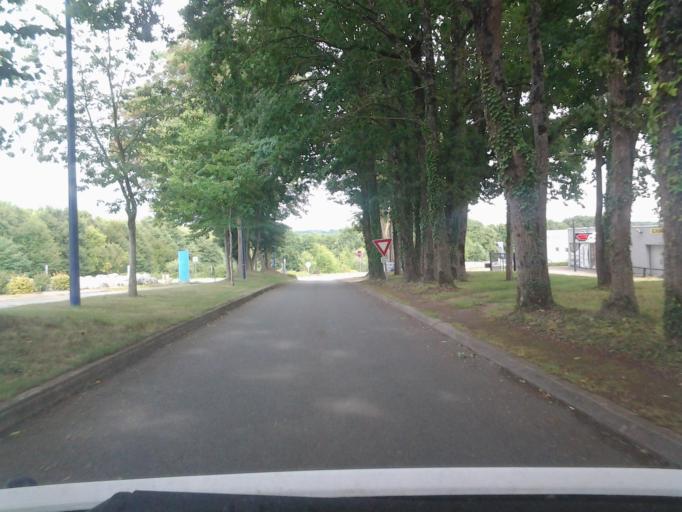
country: FR
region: Pays de la Loire
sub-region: Departement de la Vendee
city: La Roche-sur-Yon
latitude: 46.6937
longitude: -1.4260
